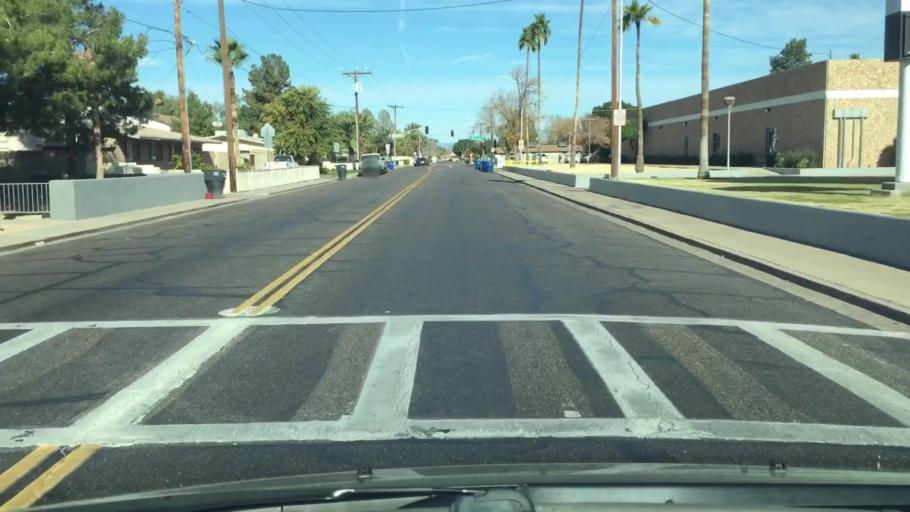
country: US
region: Arizona
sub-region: Maricopa County
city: Mesa
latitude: 33.4279
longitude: -111.8523
